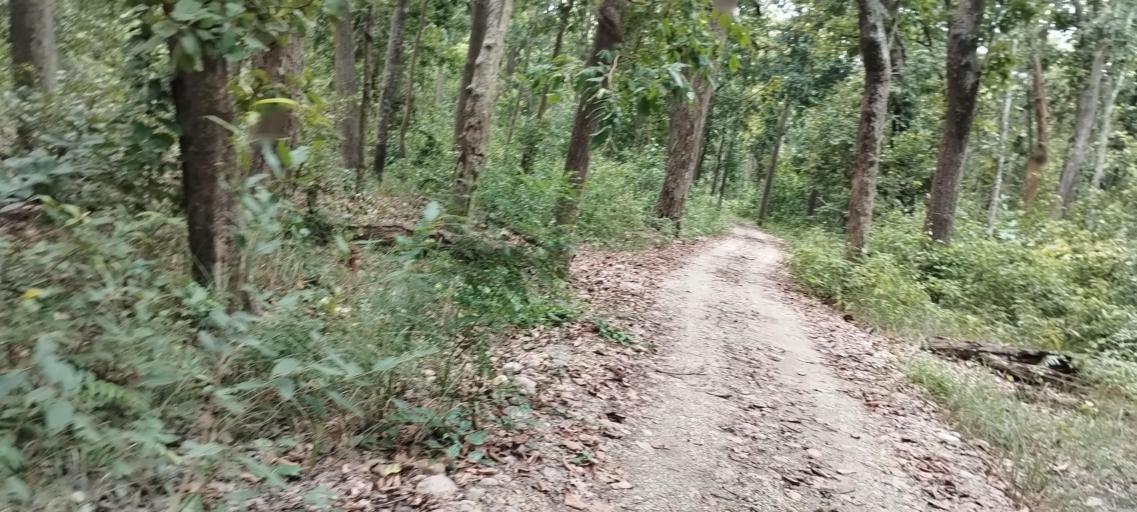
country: NP
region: Far Western
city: Tikapur
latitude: 28.4850
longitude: 81.2544
